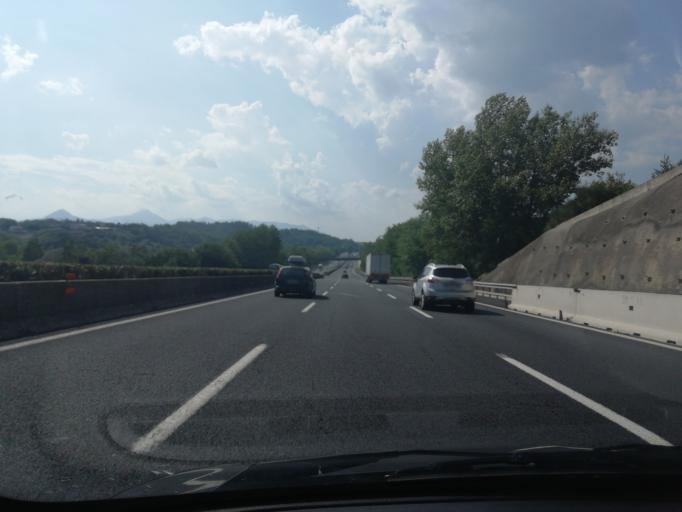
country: IT
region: Latium
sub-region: Provincia di Frosinone
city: Arnara
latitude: 41.5744
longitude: 13.3736
